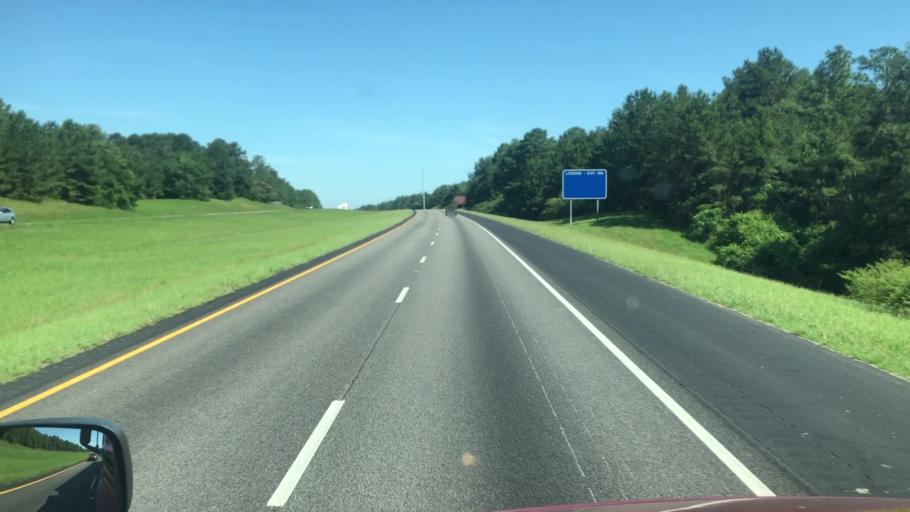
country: US
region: Alabama
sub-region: Autauga County
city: Pine Level
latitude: 32.5378
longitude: -86.4468
